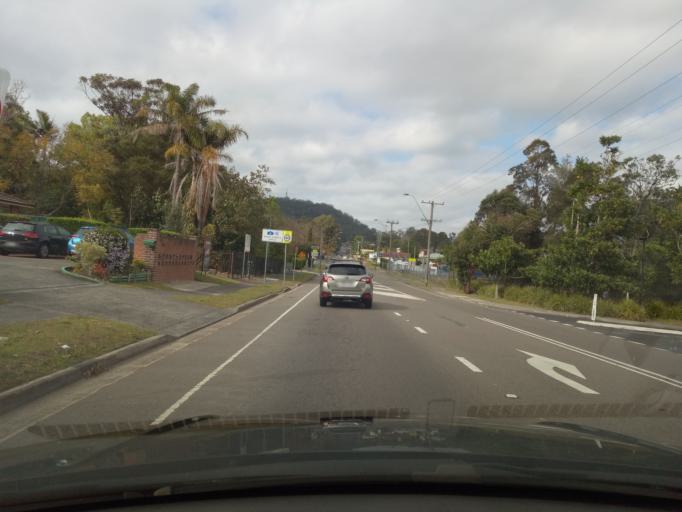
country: AU
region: New South Wales
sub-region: Gosford Shire
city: Narara
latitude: -33.4102
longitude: 151.3502
